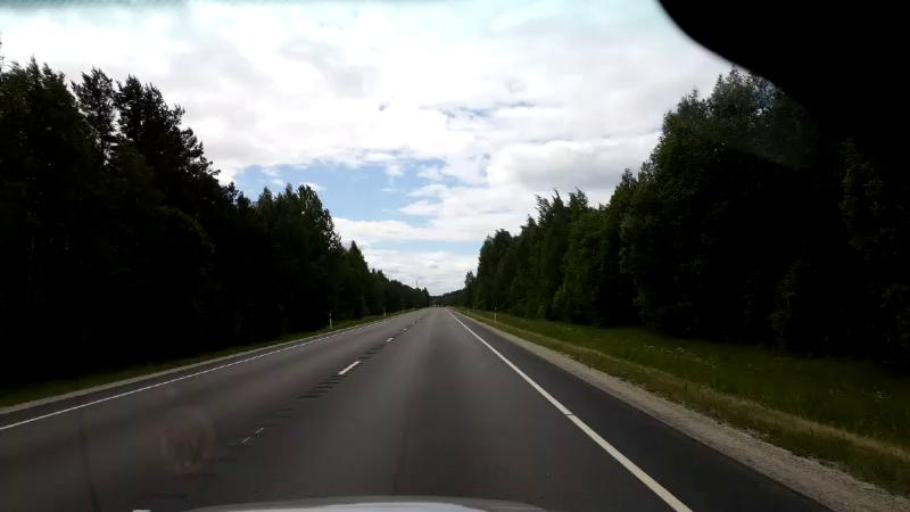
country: LV
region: Salacgrivas
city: Ainazi
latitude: 58.0967
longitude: 24.5080
